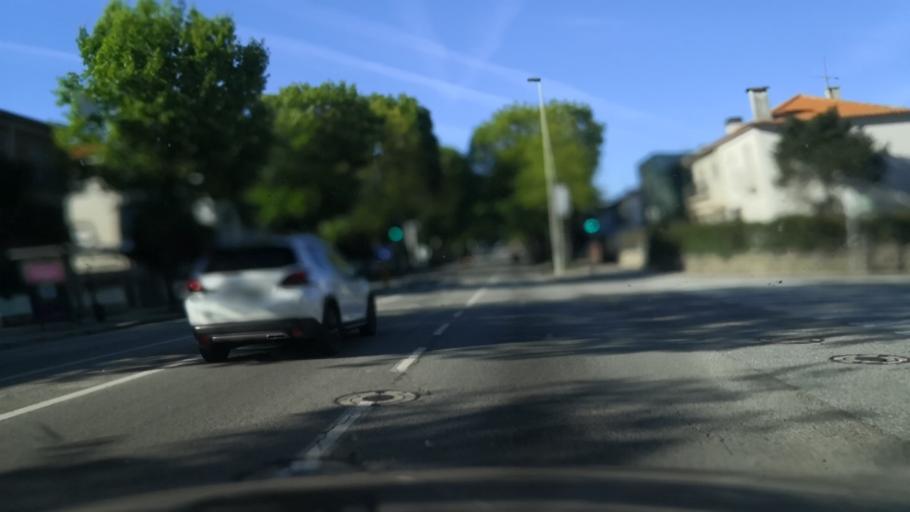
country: PT
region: Porto
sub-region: Maia
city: Pedroucos
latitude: 41.1714
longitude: -8.5860
